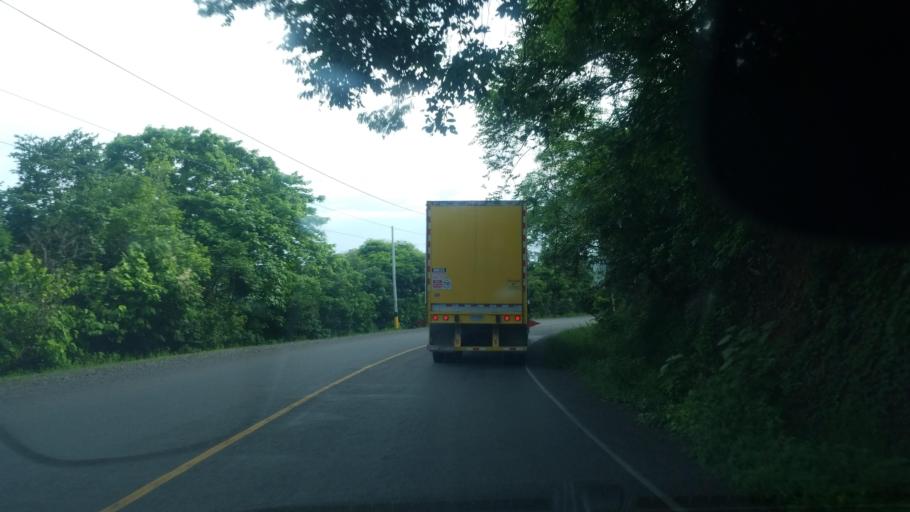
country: HN
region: Santa Barbara
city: Ilama
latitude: 15.0709
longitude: -88.2244
